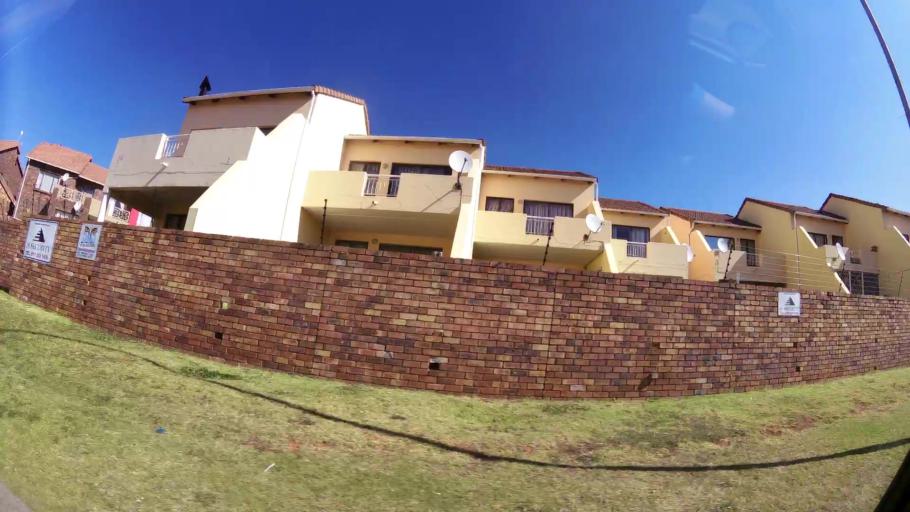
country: ZA
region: Gauteng
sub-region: City of Johannesburg Metropolitan Municipality
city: Johannesburg
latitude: -26.2659
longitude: 27.9874
